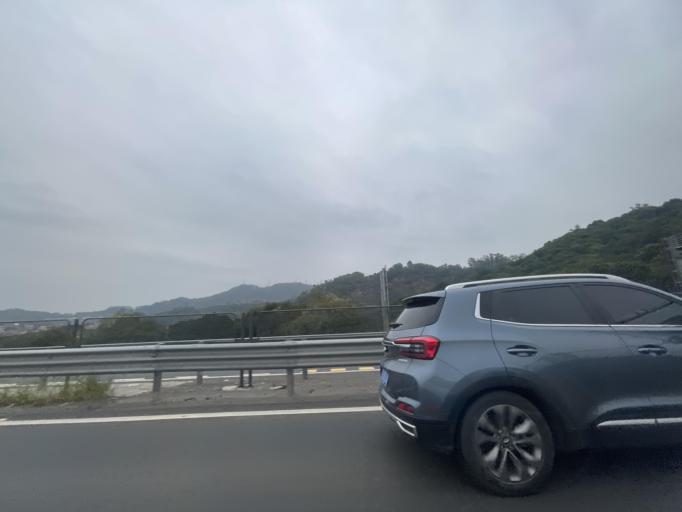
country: CN
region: Guangdong
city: Nansha
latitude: 22.7669
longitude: 113.5574
